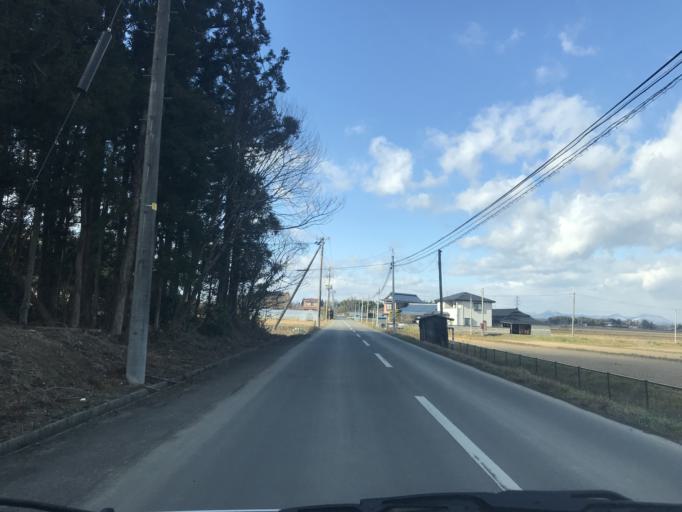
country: JP
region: Miyagi
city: Kogota
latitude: 38.7383
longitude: 141.0594
